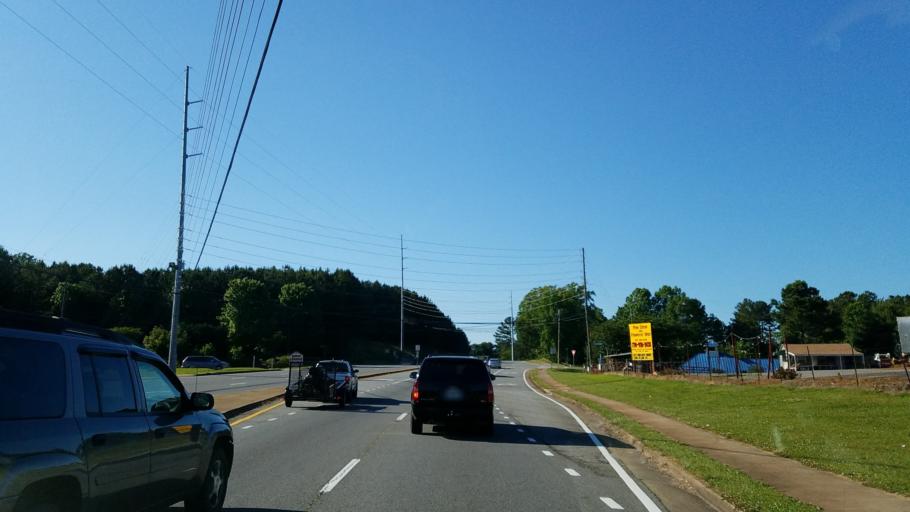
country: US
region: Georgia
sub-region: Cherokee County
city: Woodstock
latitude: 34.1146
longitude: -84.5826
